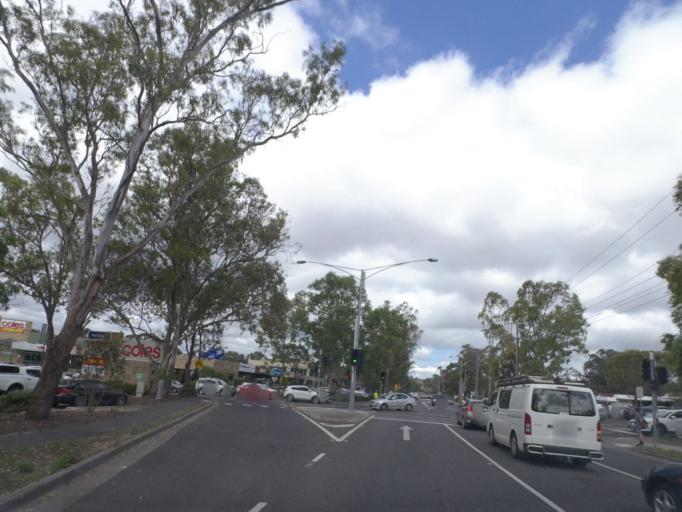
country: AU
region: Victoria
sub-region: Nillumbik
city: Diamond Creek
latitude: -37.6741
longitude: 145.1586
